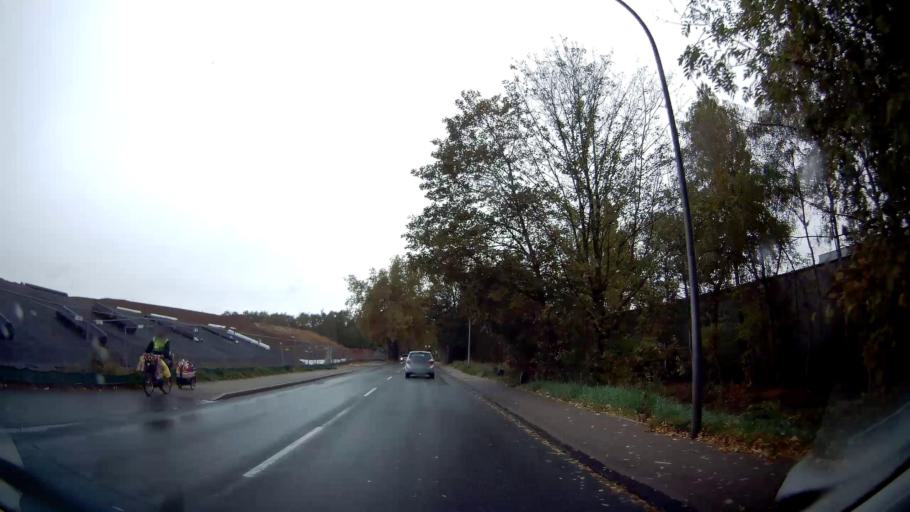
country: DE
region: North Rhine-Westphalia
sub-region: Regierungsbezirk Munster
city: Gelsenkirchen
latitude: 51.5421
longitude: 7.0847
